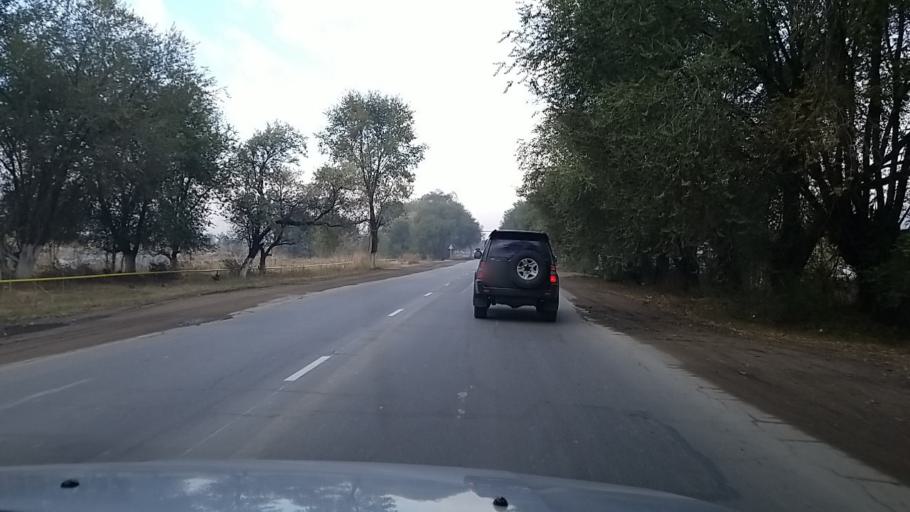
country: KZ
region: Almaty Oblysy
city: Burunday
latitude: 43.3595
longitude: 76.7531
